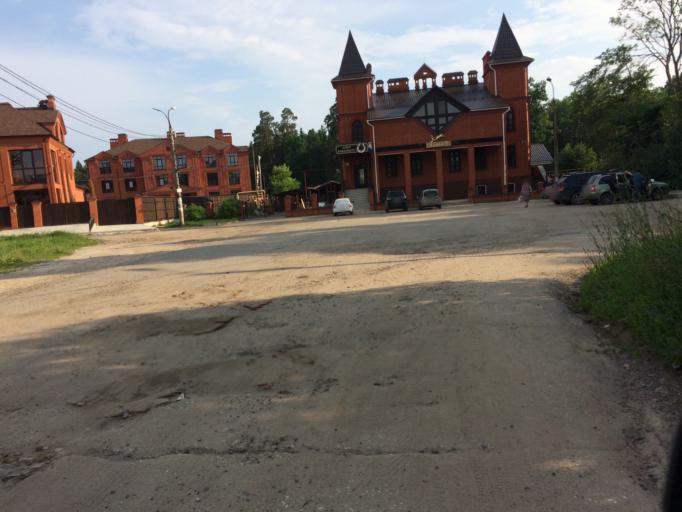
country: RU
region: Mariy-El
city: Yoshkar-Ola
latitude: 56.6175
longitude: 47.9444
